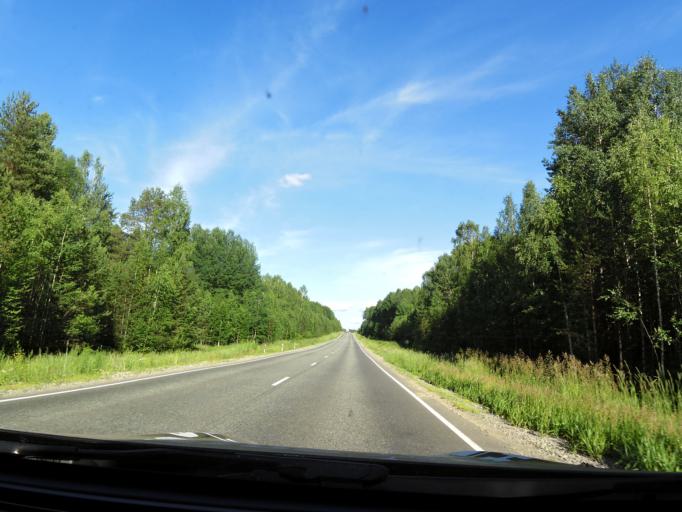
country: RU
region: Kirov
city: Chernaya Kholunitsa
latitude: 58.8621
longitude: 51.6023
